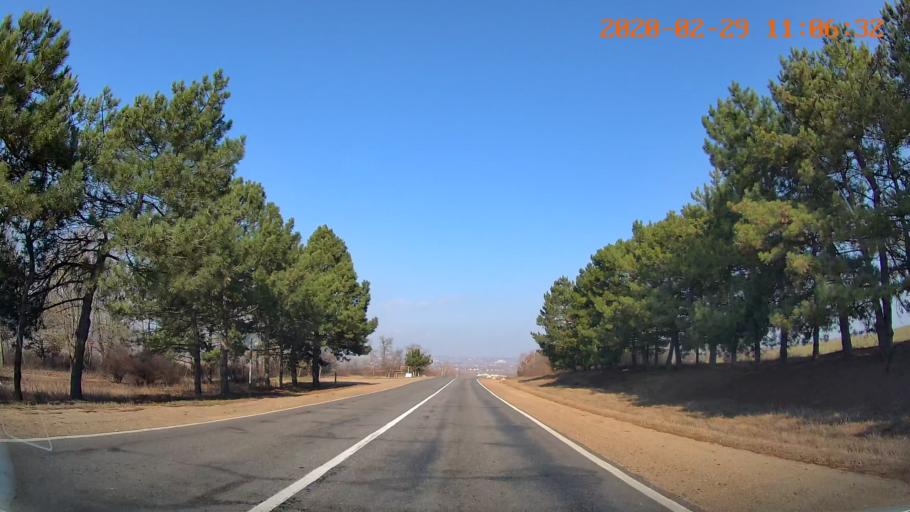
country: MD
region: Criuleni
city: Criuleni
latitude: 47.2156
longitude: 29.1876
